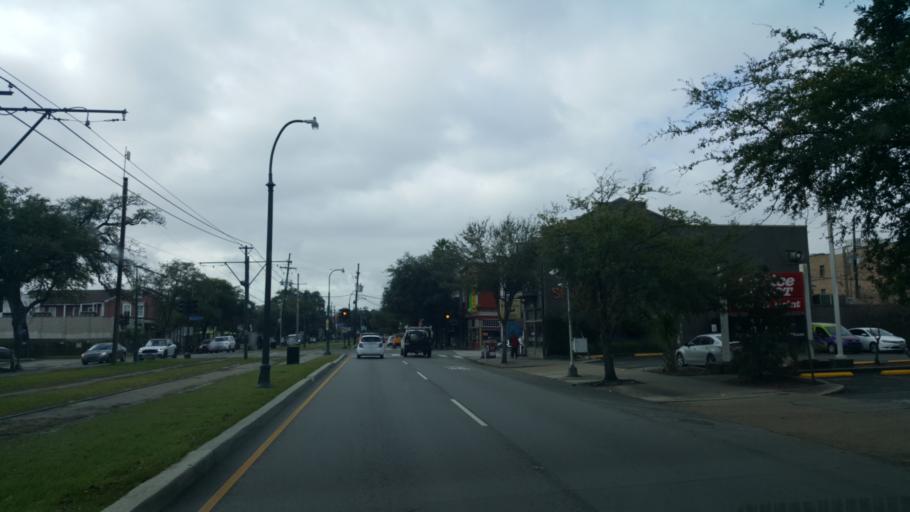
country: US
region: Louisiana
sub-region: Orleans Parish
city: New Orleans
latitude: 29.9396
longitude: -90.0752
